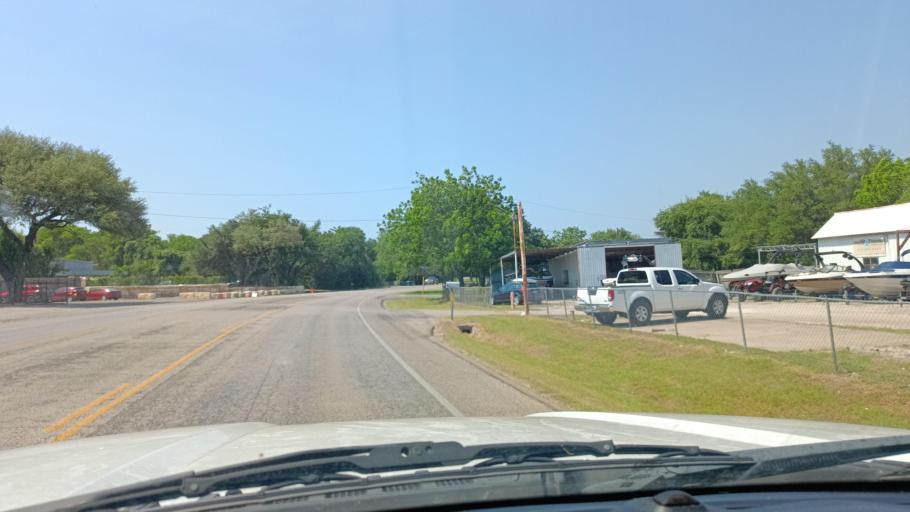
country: US
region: Texas
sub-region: Bell County
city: Morgans Point Resort
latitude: 31.1205
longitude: -97.4710
